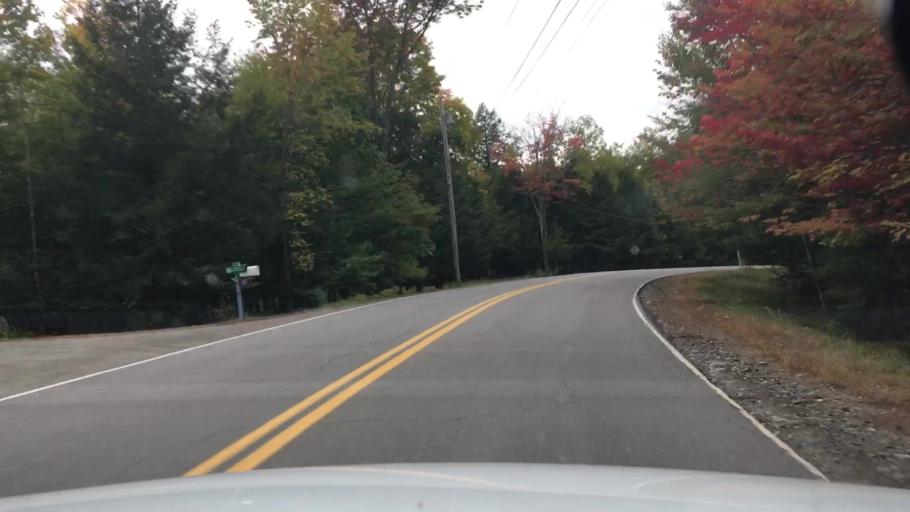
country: US
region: Maine
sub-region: Penobscot County
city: Hudson
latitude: 44.9842
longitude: -68.7889
